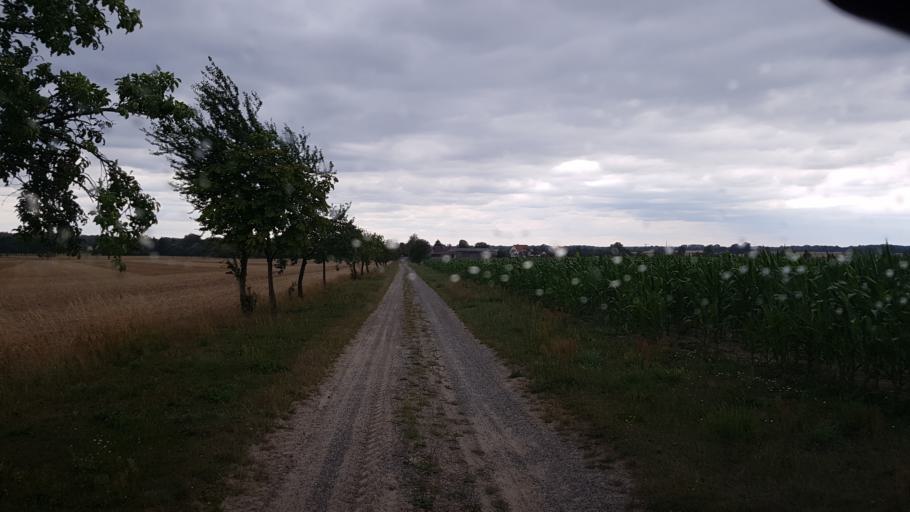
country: DE
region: Brandenburg
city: Sonnewalde
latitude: 51.7112
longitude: 13.7010
